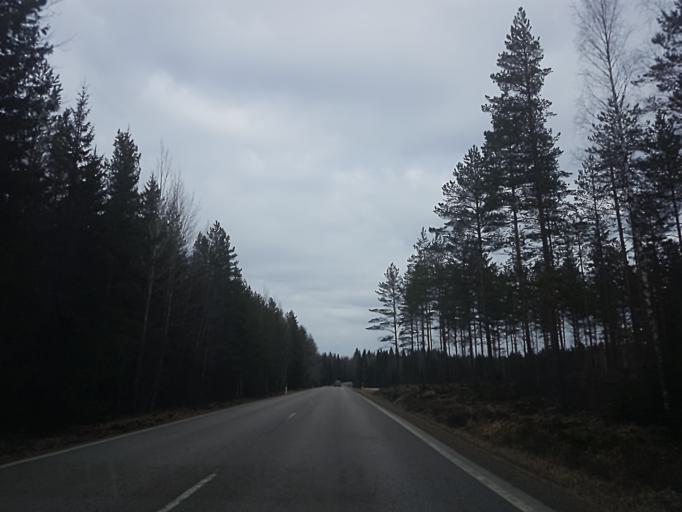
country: FI
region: South Karelia
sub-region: Lappeenranta
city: Taavetti
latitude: 60.7790
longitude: 27.3520
